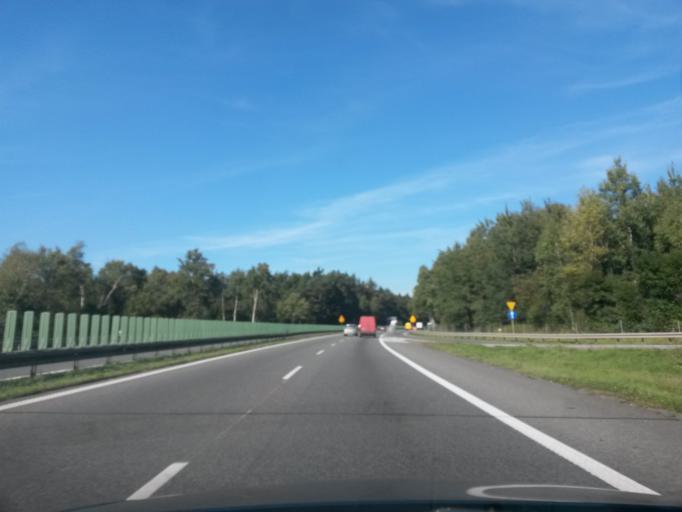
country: PL
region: Lesser Poland Voivodeship
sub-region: Krakow
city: Sidzina
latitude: 49.9986
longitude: 19.8543
